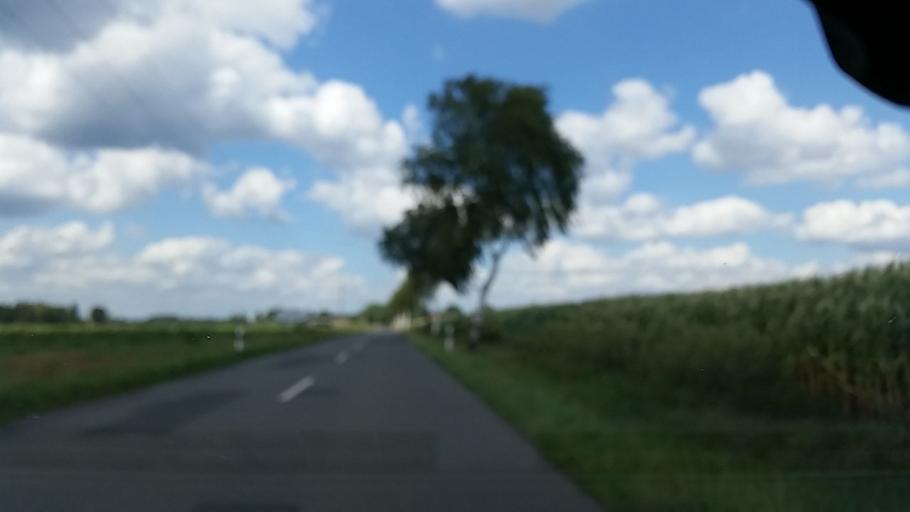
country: DE
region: Lower Saxony
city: Sprakensehl
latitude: 52.7447
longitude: 10.5147
